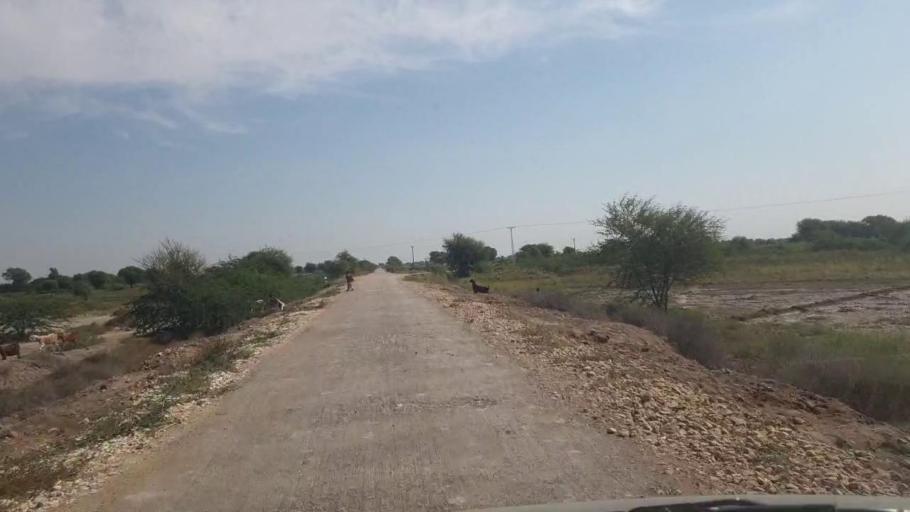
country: PK
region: Sindh
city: Tando Bago
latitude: 24.9444
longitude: 69.0890
